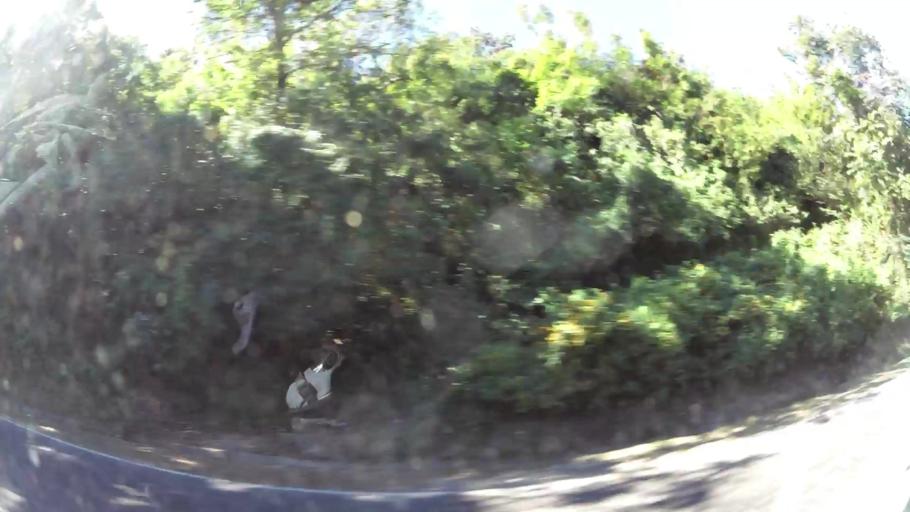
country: SV
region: Ahuachapan
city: Concepcion de Ataco
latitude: 13.8639
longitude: -89.8496
